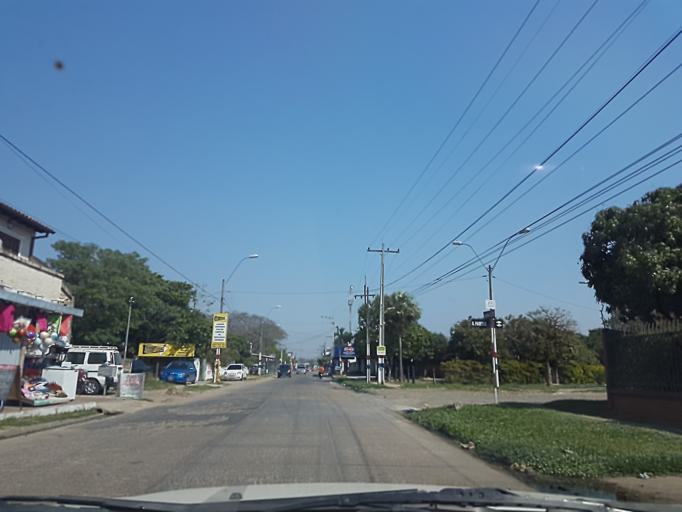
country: PY
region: Central
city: Colonia Mariano Roque Alonso
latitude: -25.2052
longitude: -57.5327
